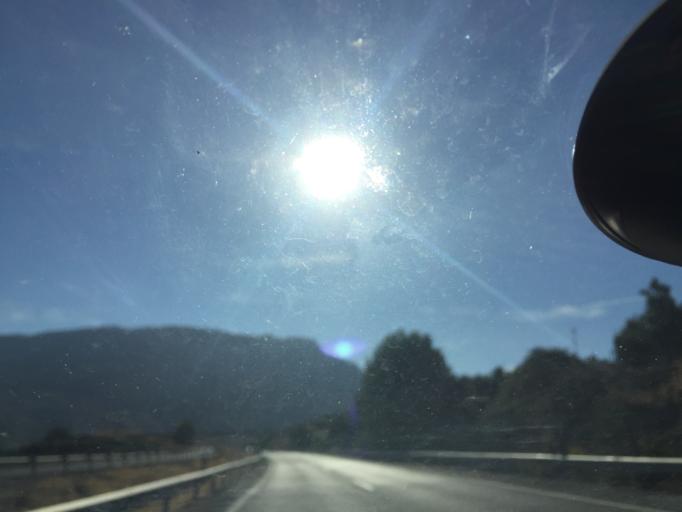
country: ES
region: Andalusia
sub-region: Provincia de Jaen
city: La Guardia de Jaen
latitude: 37.7523
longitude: -3.6965
